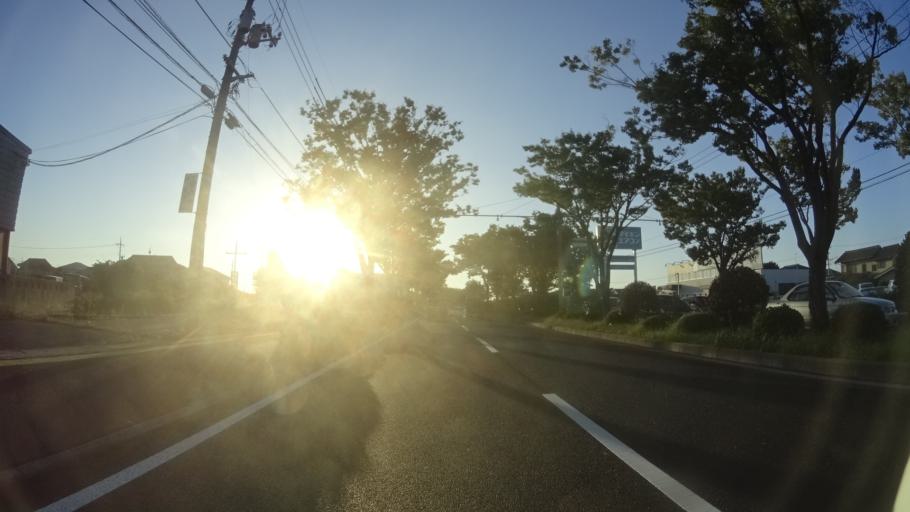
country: JP
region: Tottori
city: Yonago
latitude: 35.4517
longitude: 133.3560
